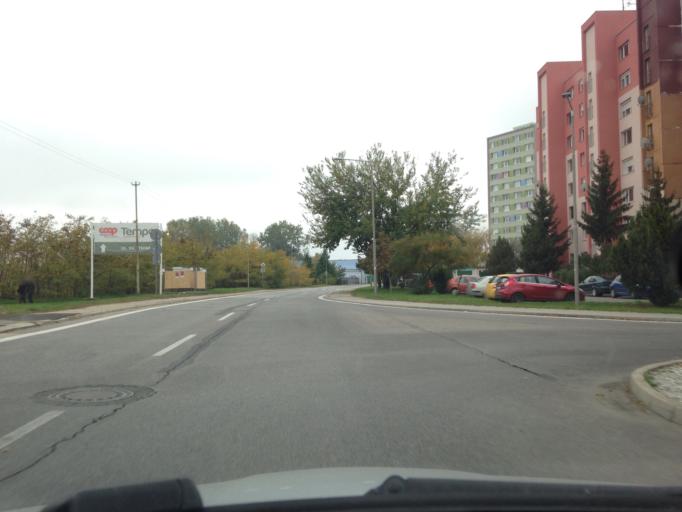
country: SK
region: Nitriansky
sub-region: Okres Nove Zamky
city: Sturovo
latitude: 47.7914
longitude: 18.7227
